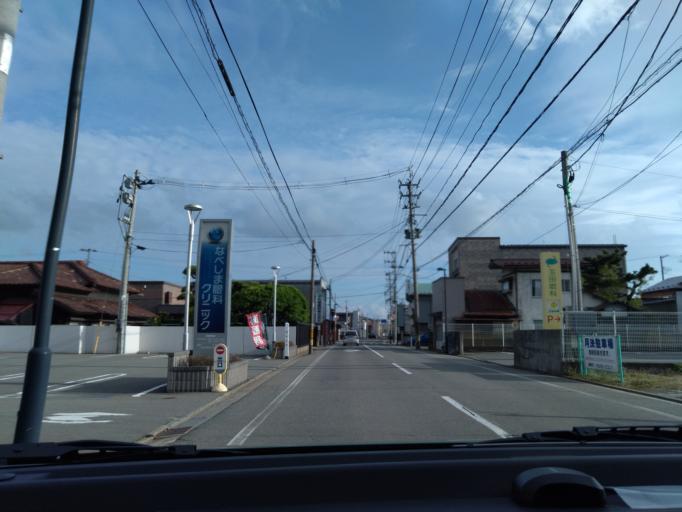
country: JP
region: Akita
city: Akita Shi
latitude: 39.7593
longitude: 140.0694
